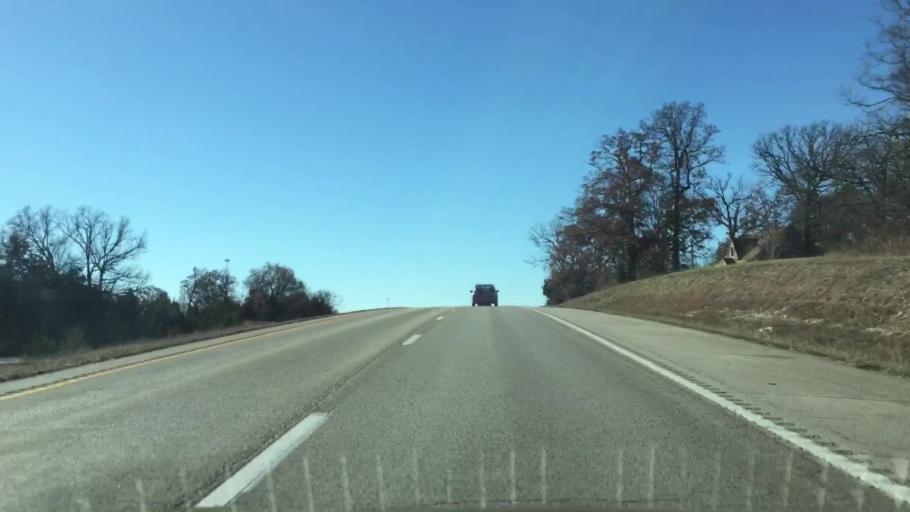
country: US
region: Missouri
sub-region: Cole County
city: Wardsville
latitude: 38.4556
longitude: -92.2991
